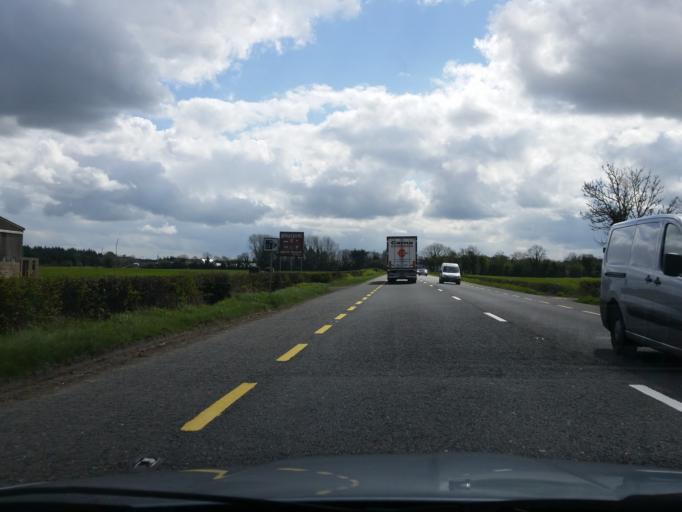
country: IE
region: Leinster
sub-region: An Mhi
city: Ratoath
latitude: 53.5786
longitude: -6.4545
